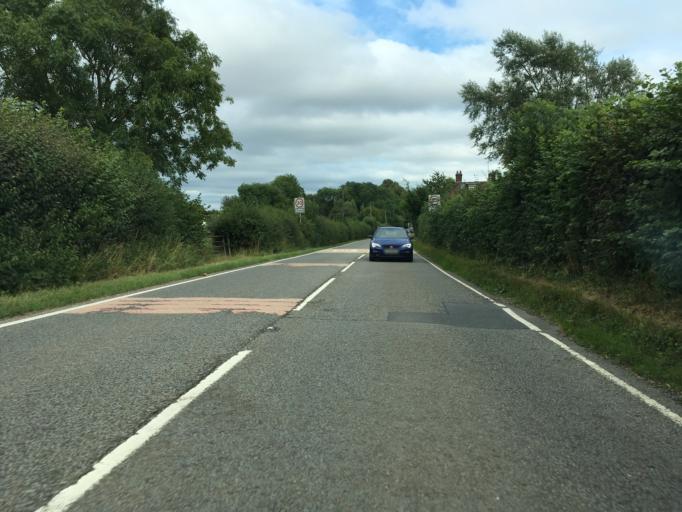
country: GB
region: England
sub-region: Hampshire
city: Petersfield
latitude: 51.0084
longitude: -0.9783
